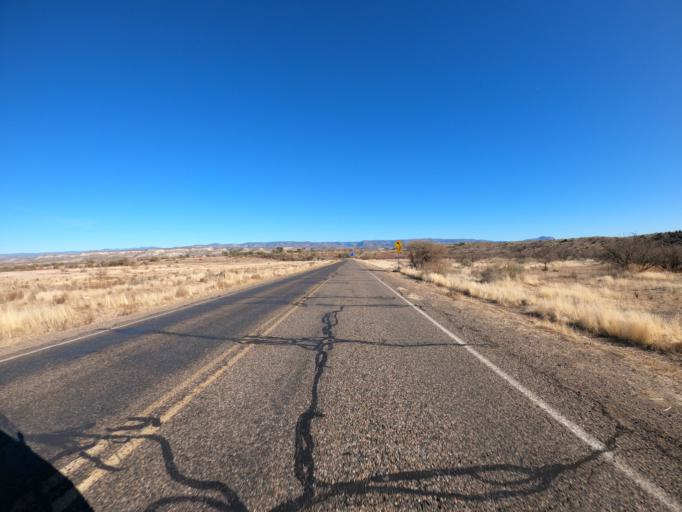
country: US
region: Arizona
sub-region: Yavapai County
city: Camp Verde
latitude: 34.5563
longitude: -111.8807
